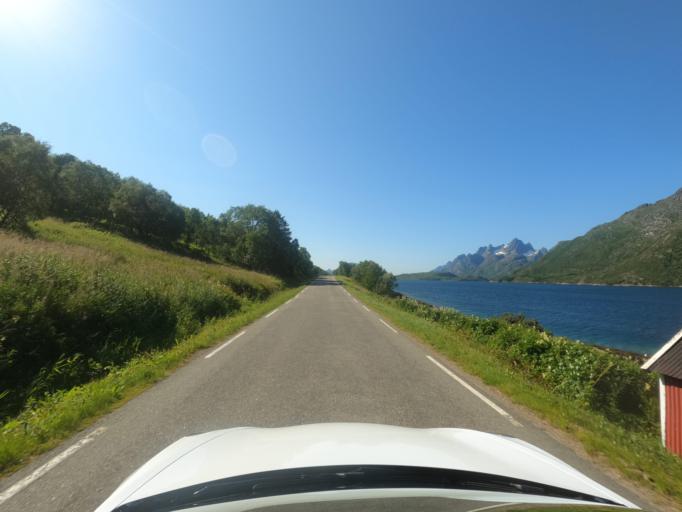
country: NO
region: Nordland
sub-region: Hadsel
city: Stokmarknes
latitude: 68.3811
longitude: 15.0885
